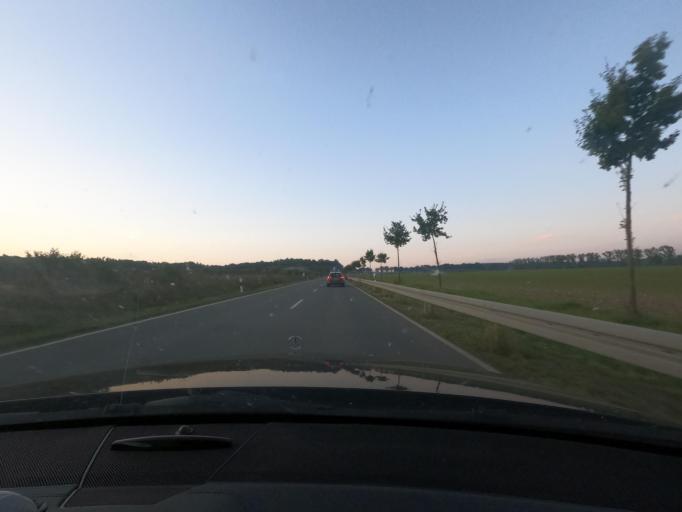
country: DE
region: North Rhine-Westphalia
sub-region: Regierungsbezirk Detmold
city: Salzkotten
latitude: 51.6256
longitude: 8.5864
